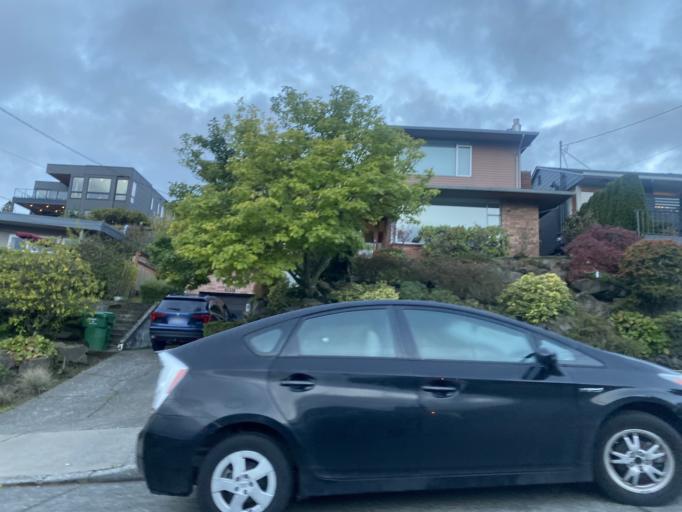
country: US
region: Washington
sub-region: King County
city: Seattle
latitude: 47.6480
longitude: -122.4047
